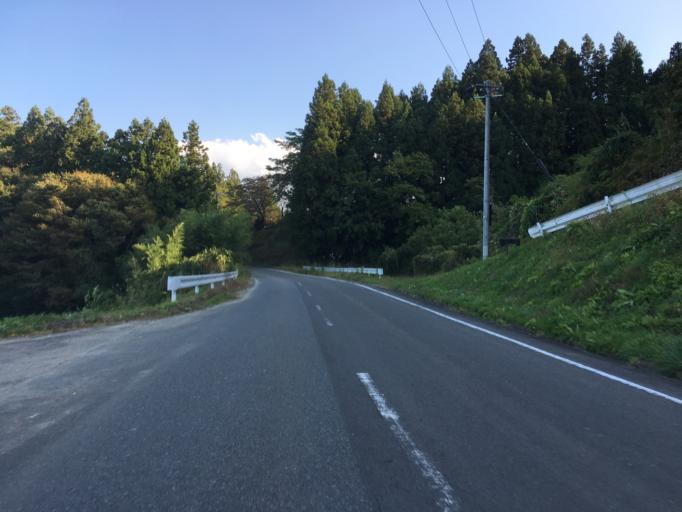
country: JP
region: Fukushima
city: Fukushima-shi
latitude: 37.6461
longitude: 140.5506
